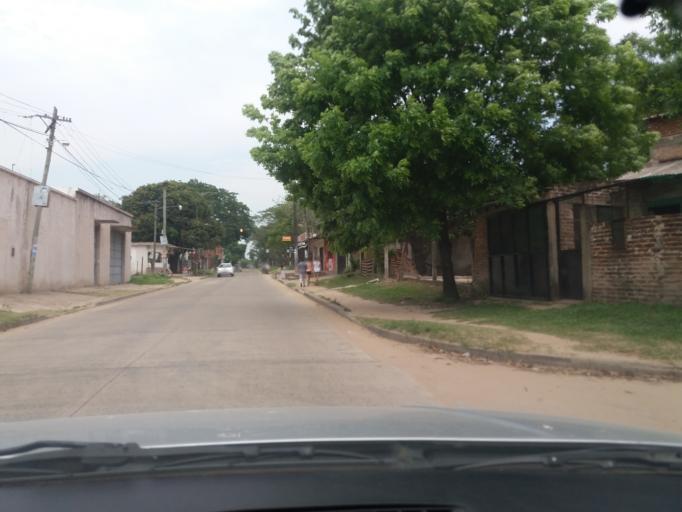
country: AR
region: Corrientes
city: Corrientes
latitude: -27.5129
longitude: -58.8046
